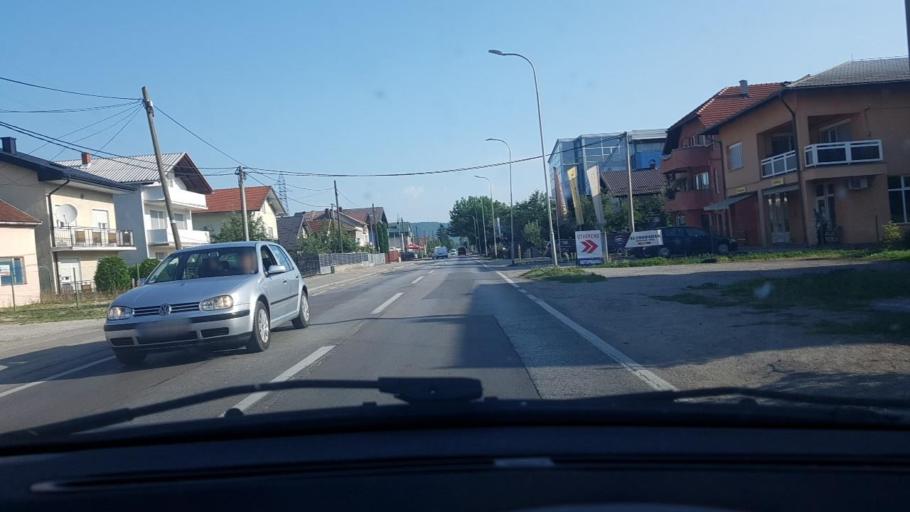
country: BA
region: Federation of Bosnia and Herzegovina
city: Bihac
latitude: 44.8247
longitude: 15.8817
